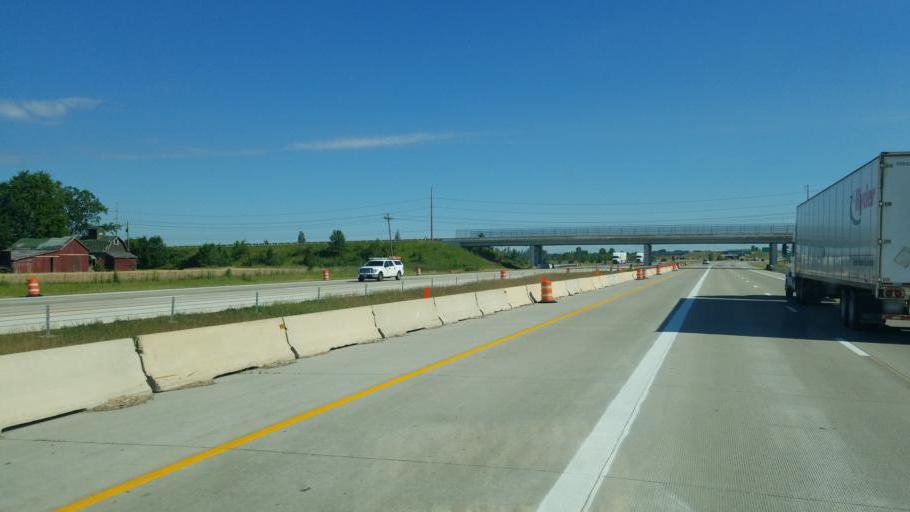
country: US
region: Ohio
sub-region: Wood County
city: Perrysburg
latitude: 41.5205
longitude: -83.6218
